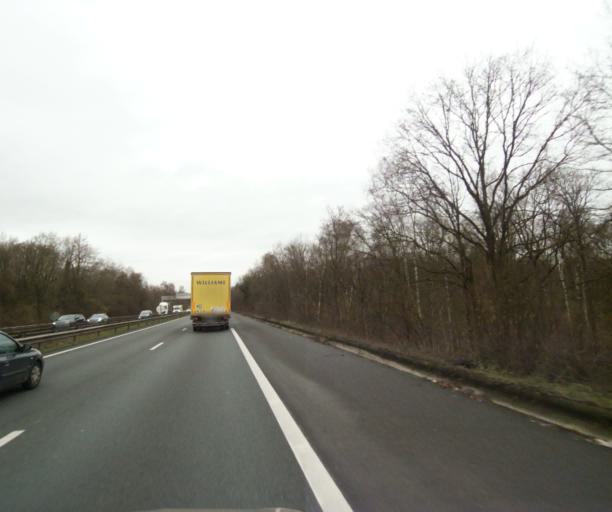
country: FR
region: Nord-Pas-de-Calais
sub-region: Departement du Nord
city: Aubry-du-Hainaut
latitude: 50.3911
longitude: 3.4546
